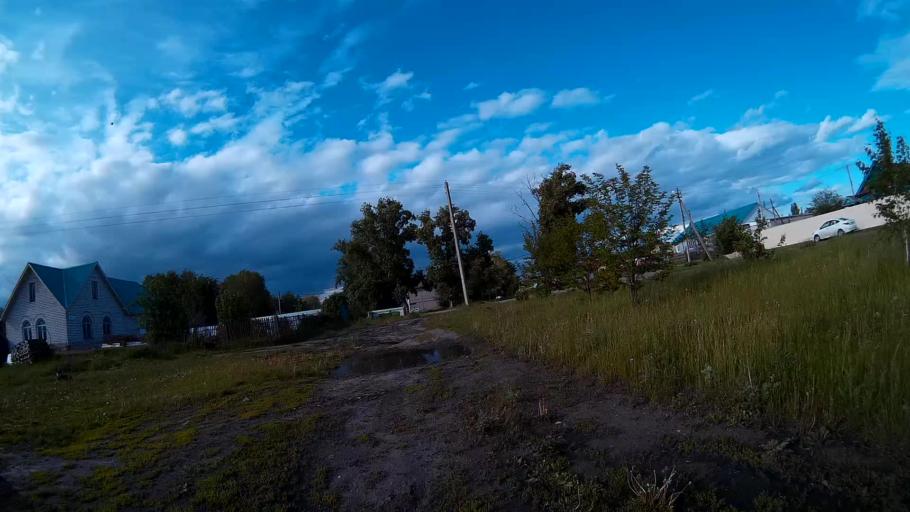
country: RU
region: Ulyanovsk
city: Novoul'yanovsk
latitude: 54.2010
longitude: 48.2674
